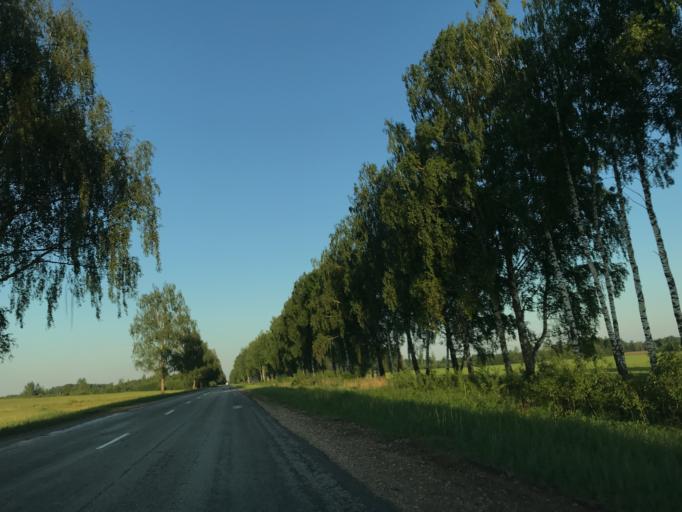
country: LV
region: Vecumnieki
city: Vecumnieki
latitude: 56.5478
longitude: 24.5998
